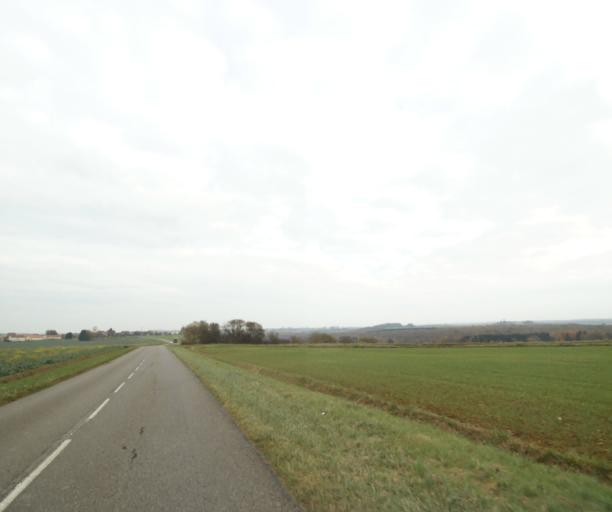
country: FR
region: Lorraine
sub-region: Departement de Meurthe-et-Moselle
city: Mancieulles
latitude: 49.2936
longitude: 5.9077
